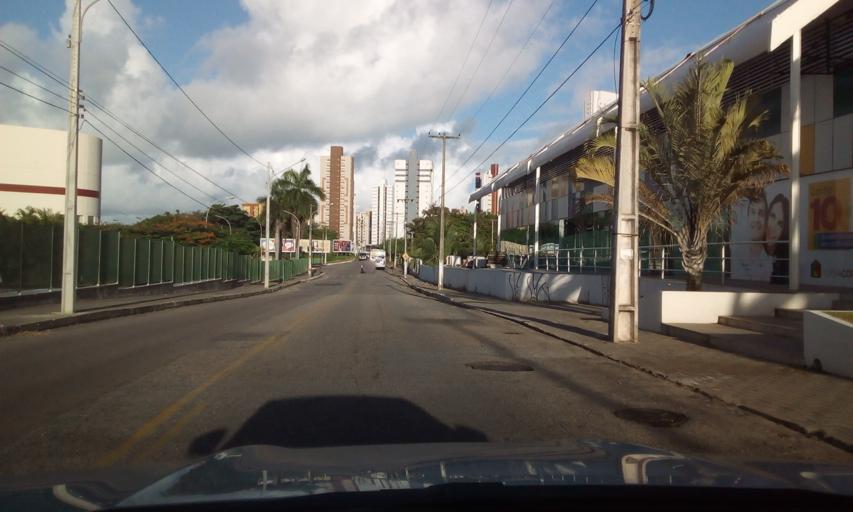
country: BR
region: Paraiba
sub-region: Joao Pessoa
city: Joao Pessoa
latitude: -7.0920
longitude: -34.8474
